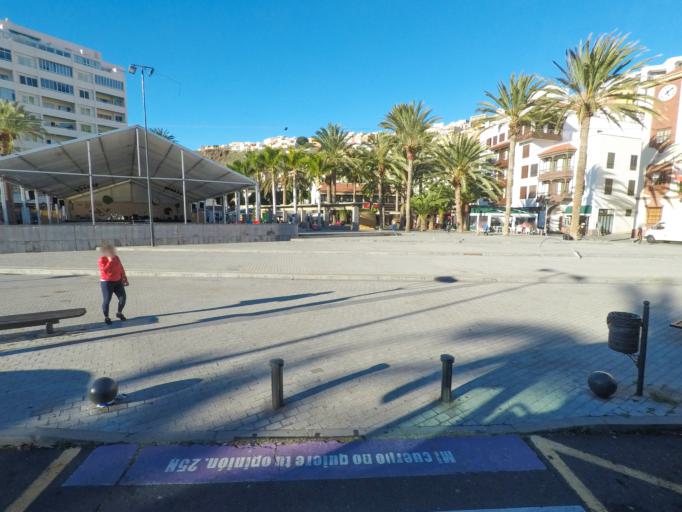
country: ES
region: Canary Islands
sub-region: Provincia de Santa Cruz de Tenerife
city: San Sebastian de la Gomera
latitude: 28.0903
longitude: -17.1100
